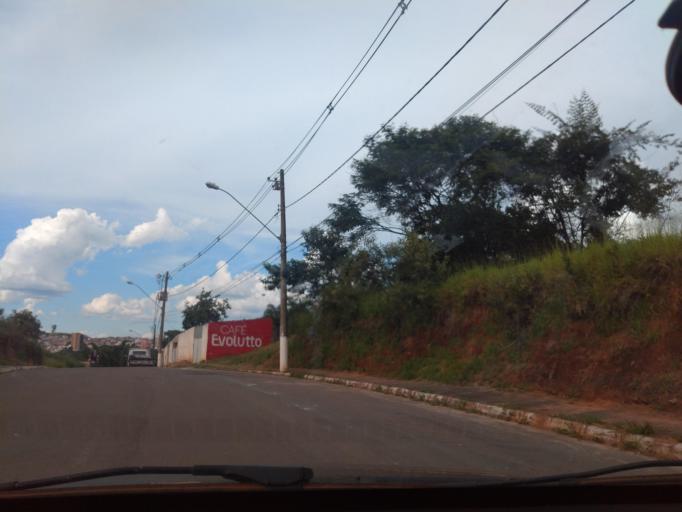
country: BR
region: Minas Gerais
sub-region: Tres Coracoes
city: Tres Coracoes
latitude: -21.7089
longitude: -45.2613
